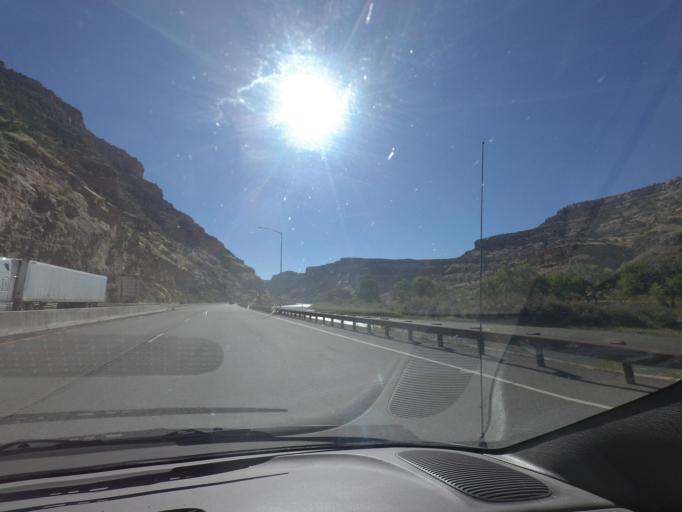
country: US
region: Colorado
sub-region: Mesa County
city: Palisade
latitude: 39.1801
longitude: -108.2842
